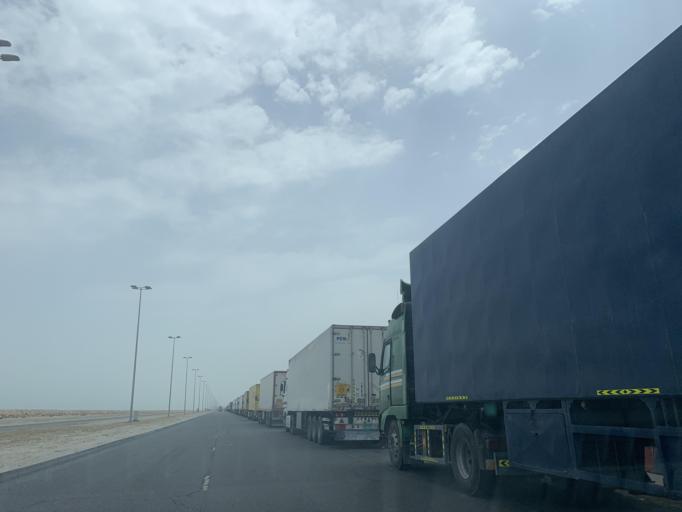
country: BH
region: Muharraq
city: Al Hadd
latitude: 26.2085
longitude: 50.7052
